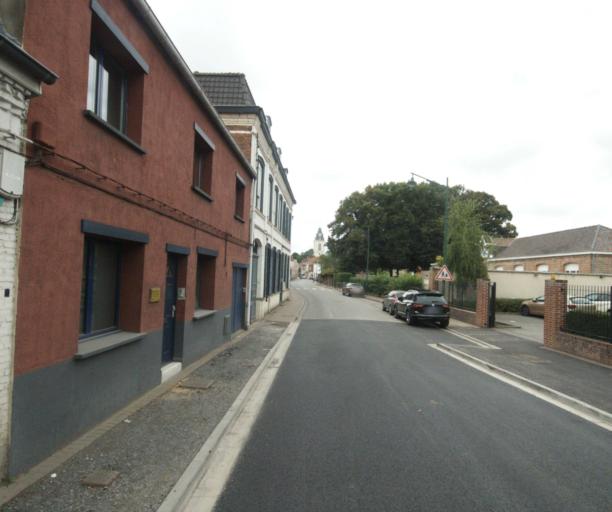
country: FR
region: Nord-Pas-de-Calais
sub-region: Departement du Nord
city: Villeneuve-d'Ascq
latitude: 50.6259
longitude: 3.1533
